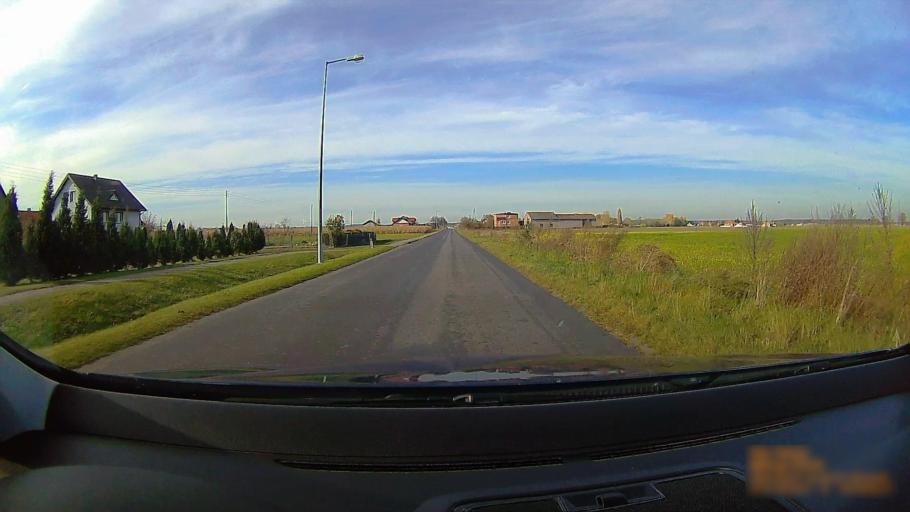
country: PL
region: Greater Poland Voivodeship
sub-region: Powiat ostrzeszowski
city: Doruchow
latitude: 51.4220
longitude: 18.0624
